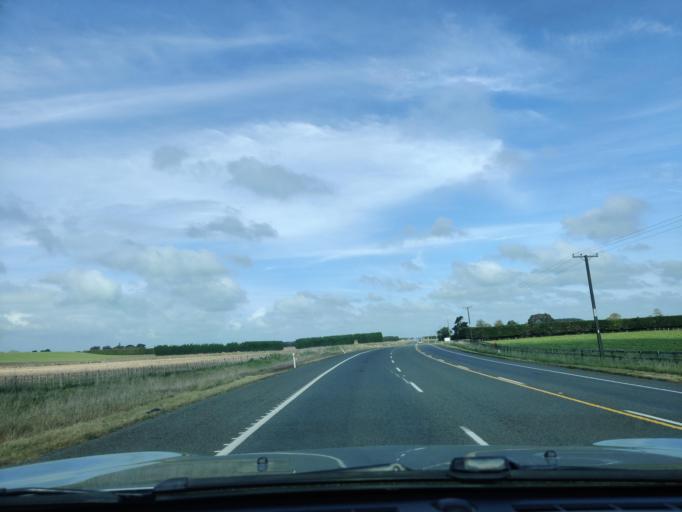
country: NZ
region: Manawatu-Wanganui
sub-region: Wanganui District
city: Wanganui
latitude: -39.9827
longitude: 175.1505
